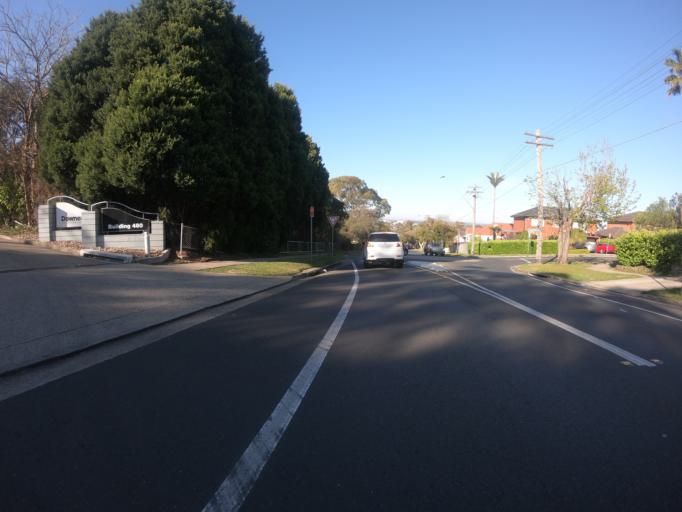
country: AU
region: New South Wales
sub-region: Hunters Hill
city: Gladesville
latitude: -33.8234
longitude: 151.1212
